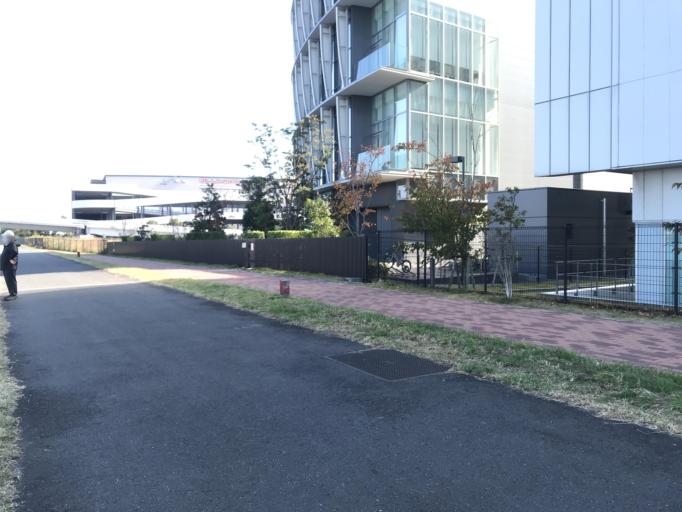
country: JP
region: Kanagawa
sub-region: Kawasaki-shi
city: Kawasaki
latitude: 35.5403
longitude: 139.7586
